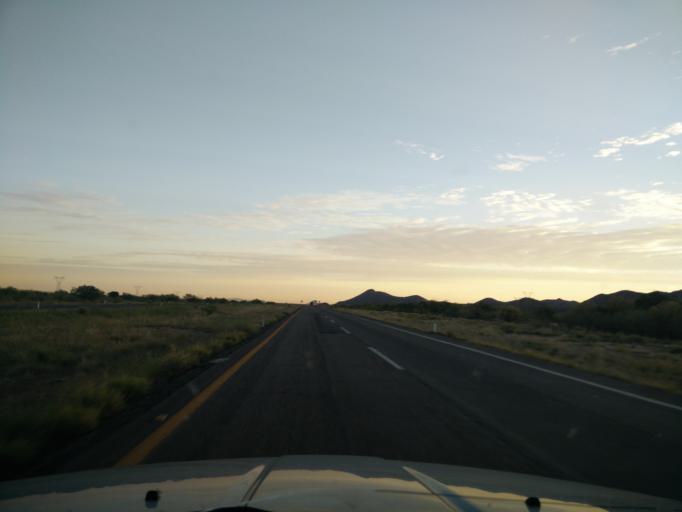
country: MX
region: Sonora
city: Hermosillo
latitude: 28.5959
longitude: -111.0231
